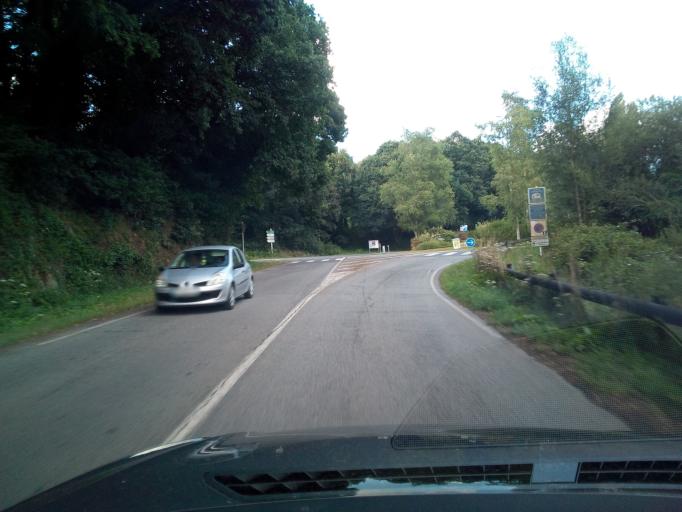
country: FR
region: Brittany
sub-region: Departement du Finistere
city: Landivisiau
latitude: 48.5043
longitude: -4.0869
